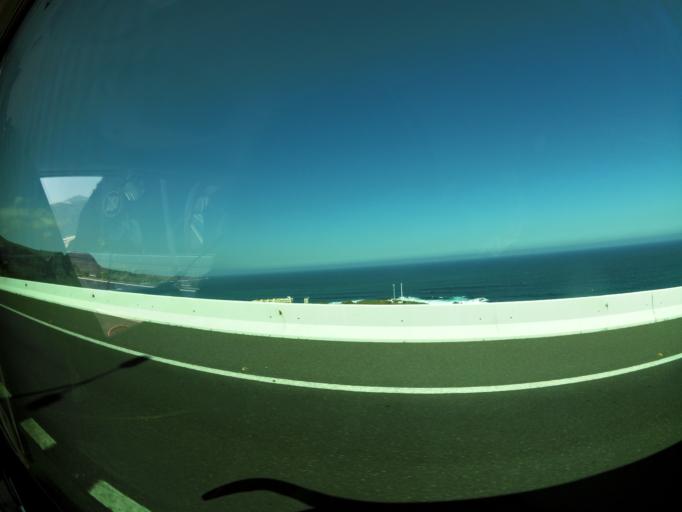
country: ES
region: Canary Islands
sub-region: Provincia de Las Palmas
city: Moya
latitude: 28.1426
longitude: -15.5850
